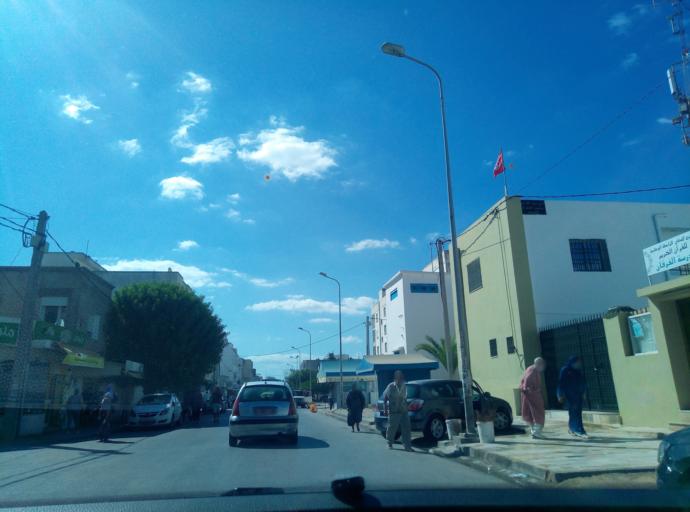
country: TN
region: Tunis
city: La Goulette
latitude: 36.8517
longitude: 10.2621
